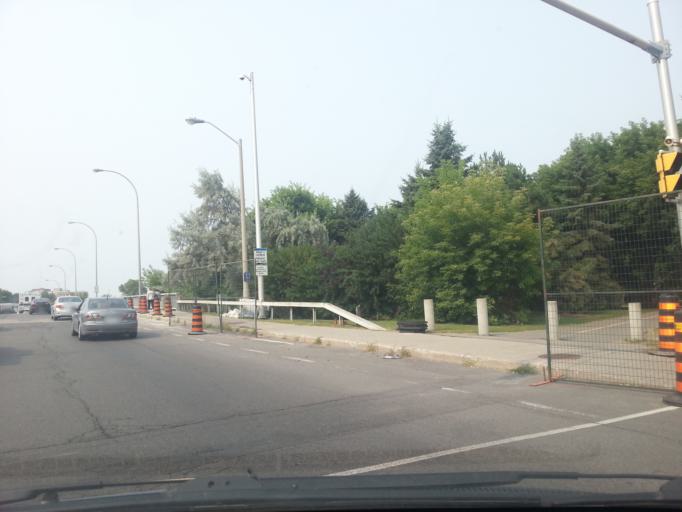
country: CA
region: Ontario
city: Ottawa
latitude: 45.4383
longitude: -75.6779
